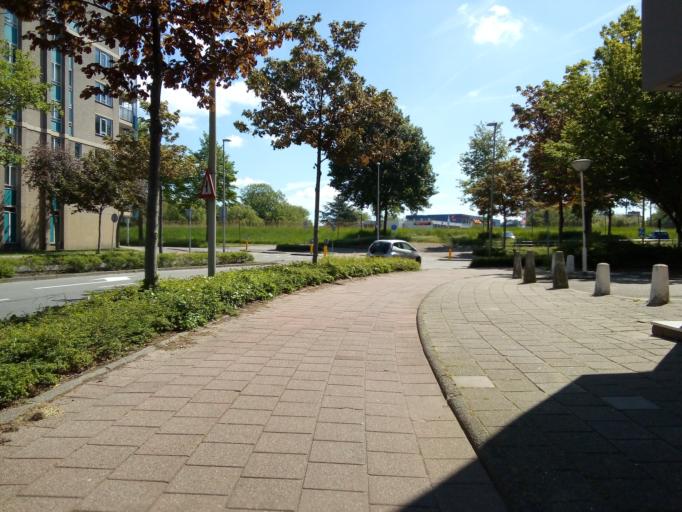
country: NL
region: South Holland
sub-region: Gemeente Zoetermeer
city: Zoetermeer
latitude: 52.0621
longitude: 4.4975
